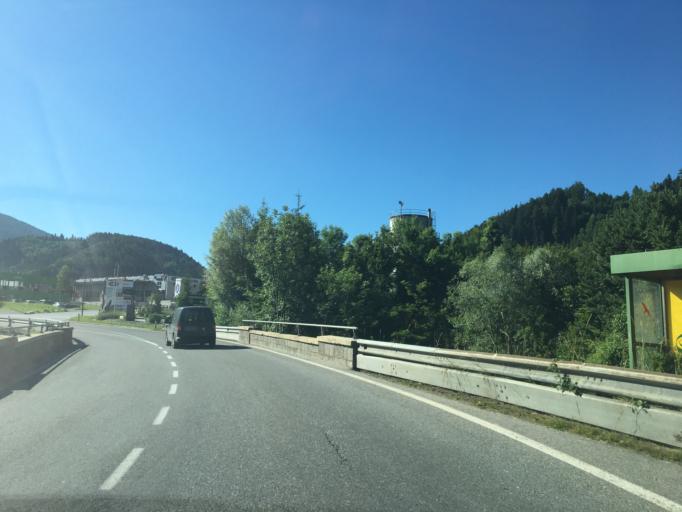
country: AT
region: Tyrol
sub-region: Politischer Bezirk Innsbruck Land
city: Mutters
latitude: 47.2302
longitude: 11.3847
